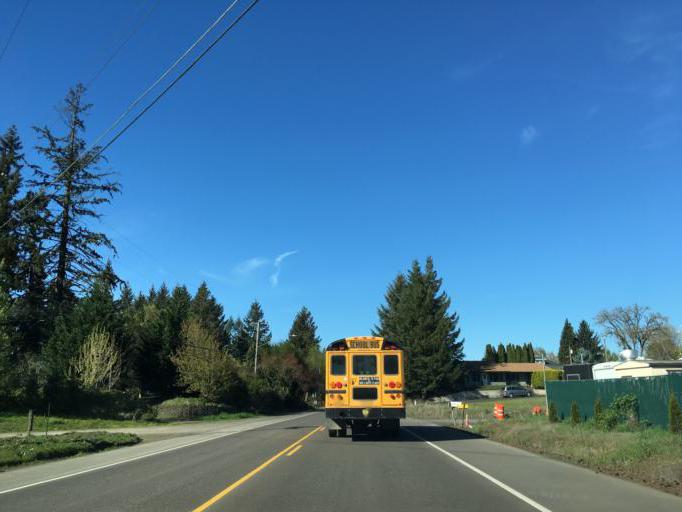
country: US
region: Oregon
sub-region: Marion County
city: Hubbard
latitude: 45.2258
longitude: -122.7579
